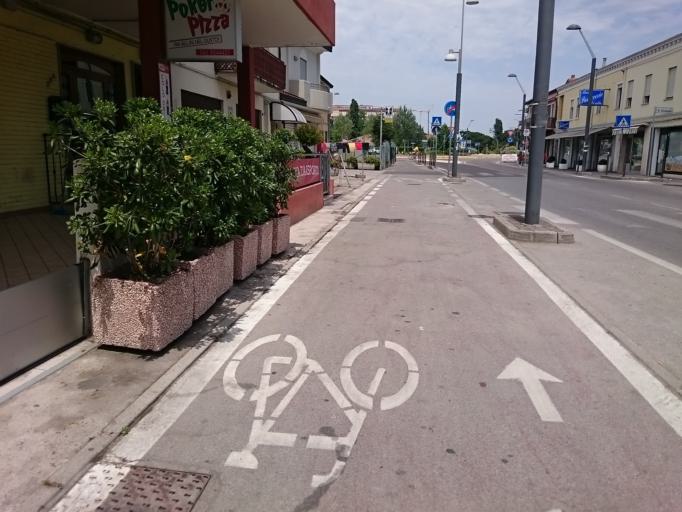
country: IT
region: Veneto
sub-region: Provincia di Venezia
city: Chioggia
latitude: 45.1952
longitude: 12.2822
